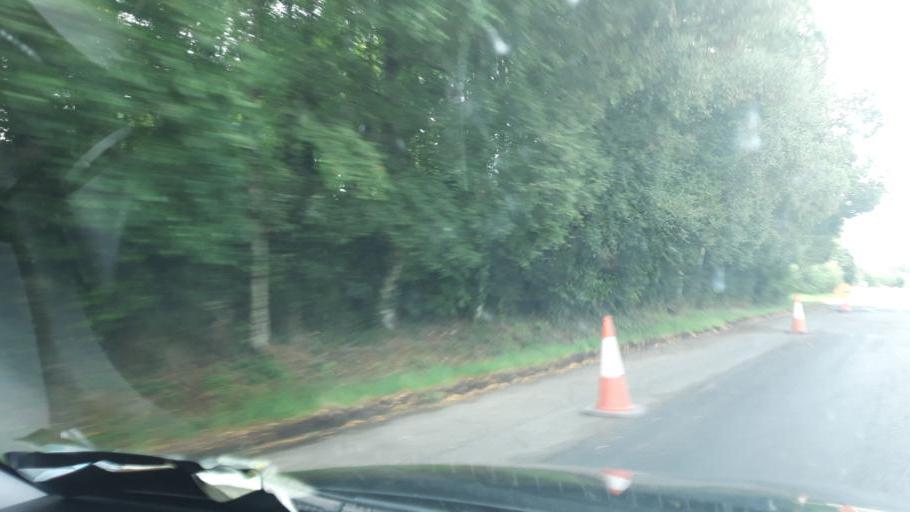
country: IE
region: Leinster
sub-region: Kilkenny
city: Callan
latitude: 52.5561
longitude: -7.3741
